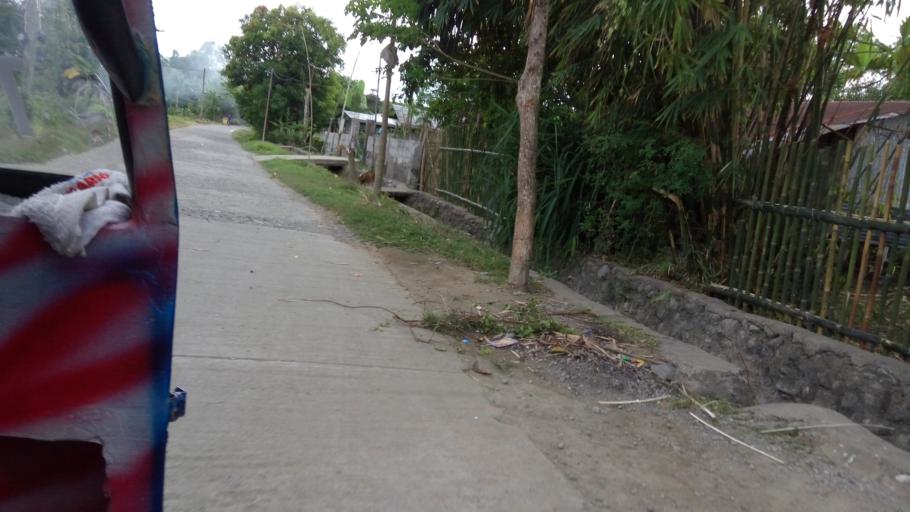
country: PH
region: Ilocos
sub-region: Province of La Union
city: Santo Tomas
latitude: 16.2898
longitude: 120.3794
